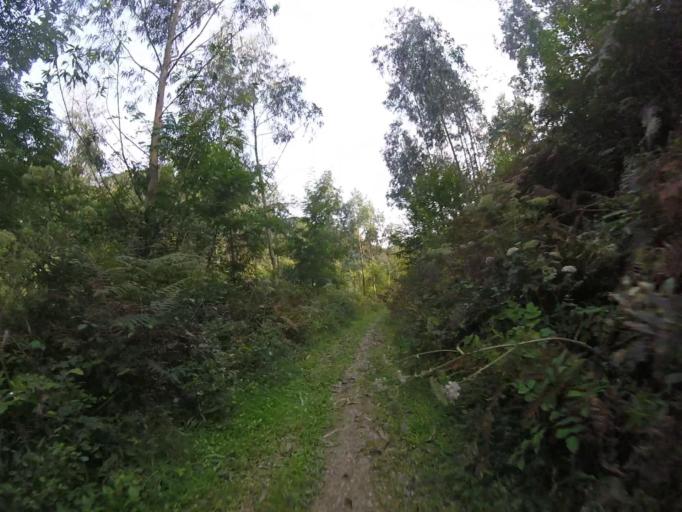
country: ES
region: Navarre
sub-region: Provincia de Navarra
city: Arano
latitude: 43.2300
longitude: -1.9330
